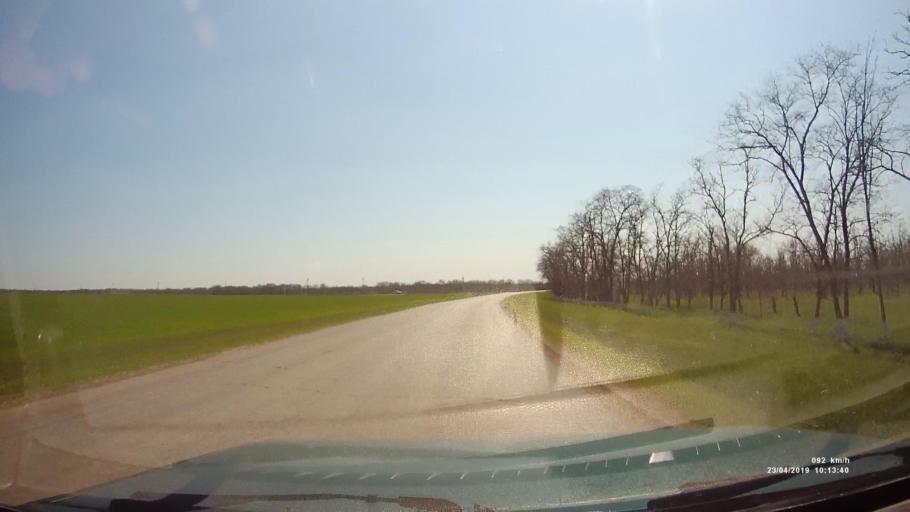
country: RU
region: Rostov
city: Sovetskoye
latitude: 46.6836
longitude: 42.3598
